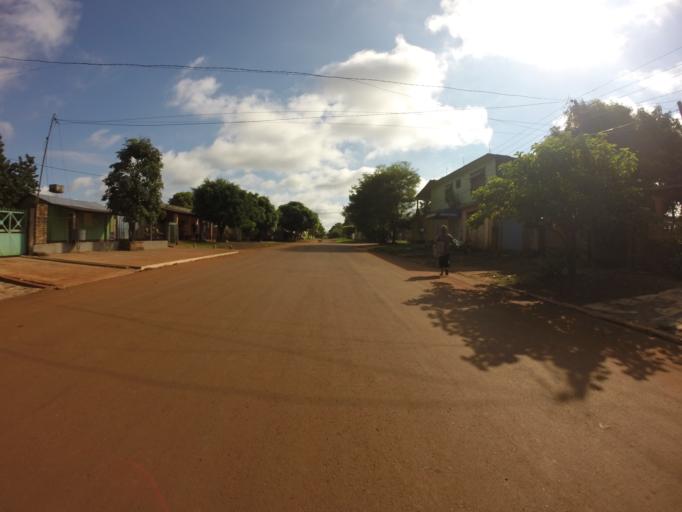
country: PY
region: Alto Parana
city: Ciudad del Este
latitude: -25.4006
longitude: -54.6460
